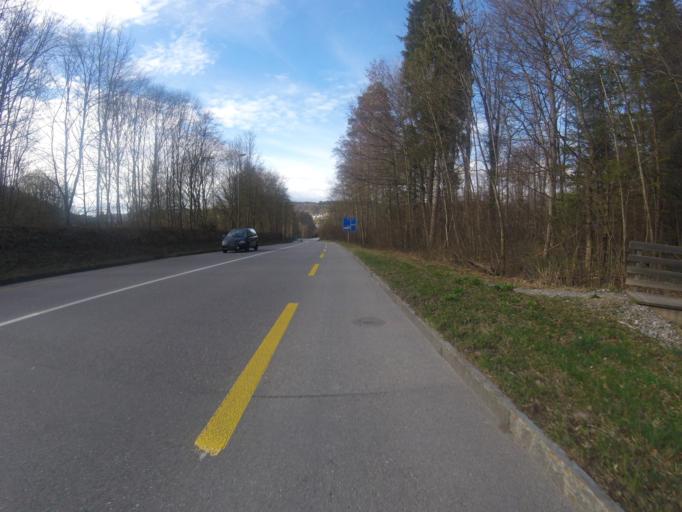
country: CH
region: Bern
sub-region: Bern-Mittelland District
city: Wohlen
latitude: 46.9600
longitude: 7.3876
